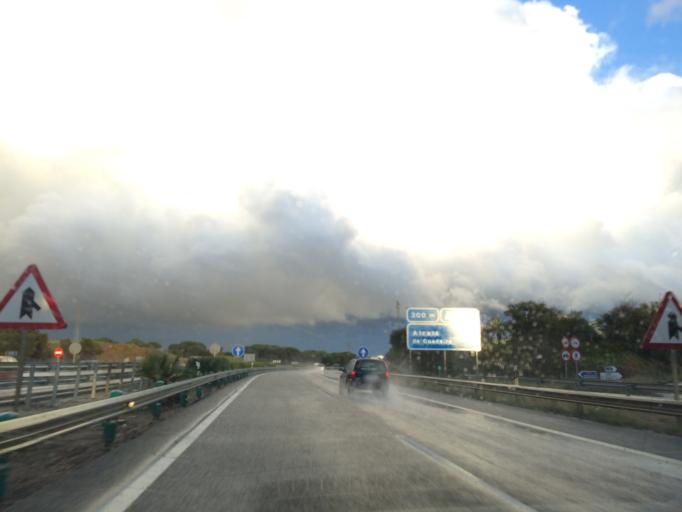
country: ES
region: Andalusia
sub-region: Provincia de Sevilla
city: Alcala de Guadaira
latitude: 37.3464
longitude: -5.8257
